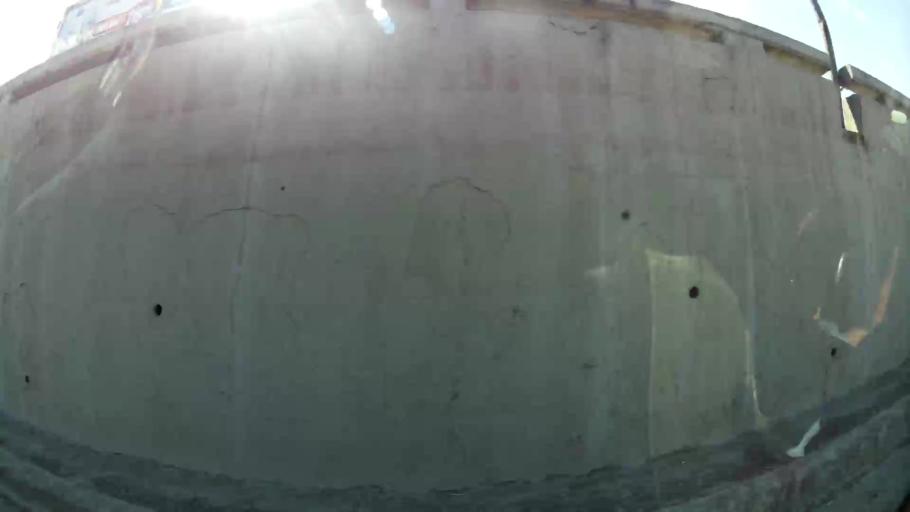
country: EC
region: Guayas
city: Santa Lucia
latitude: -2.1007
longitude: -79.9359
